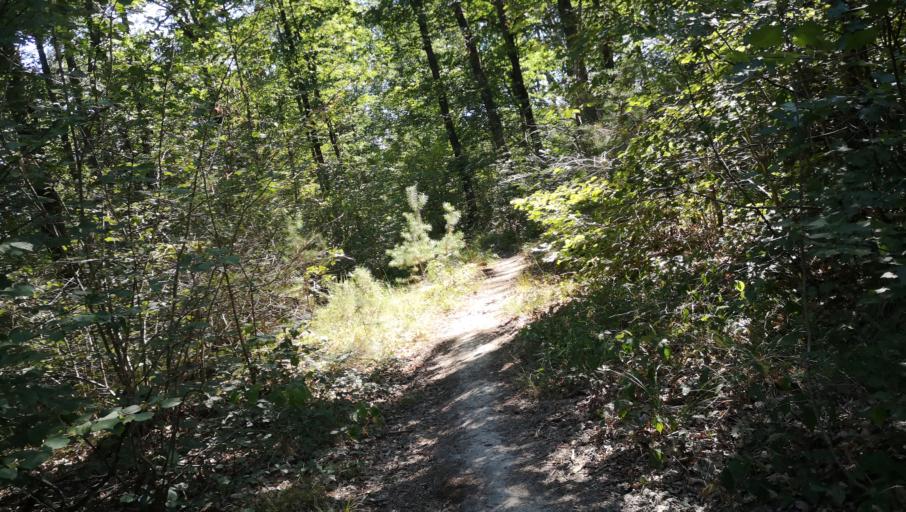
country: FR
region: Centre
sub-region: Departement du Loiret
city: Semoy
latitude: 47.9487
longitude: 1.9539
